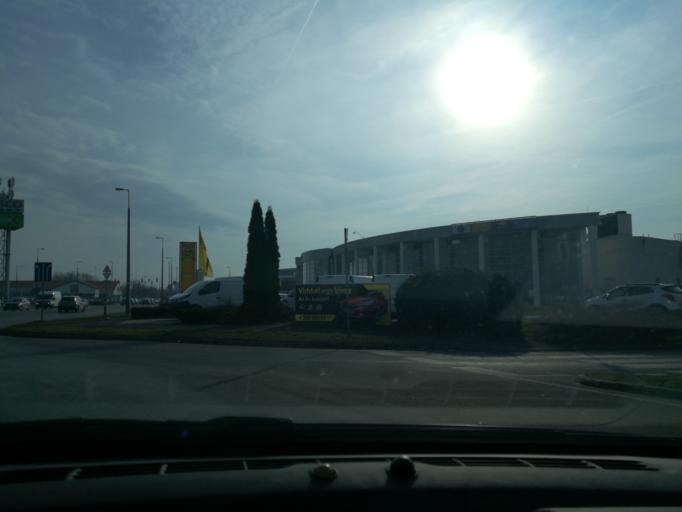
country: HU
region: Szabolcs-Szatmar-Bereg
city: Nyiregyhaza
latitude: 47.9708
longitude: 21.7364
